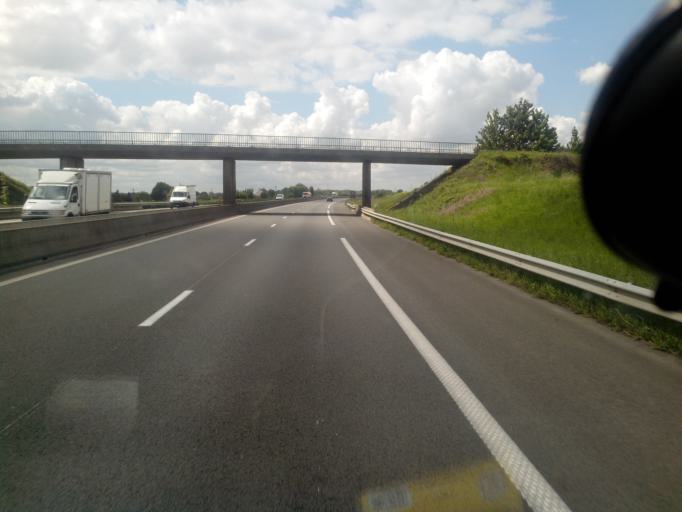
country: FR
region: Nord-Pas-de-Calais
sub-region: Departement du Nord
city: Godewaersvelde
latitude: 50.7537
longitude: 2.6555
